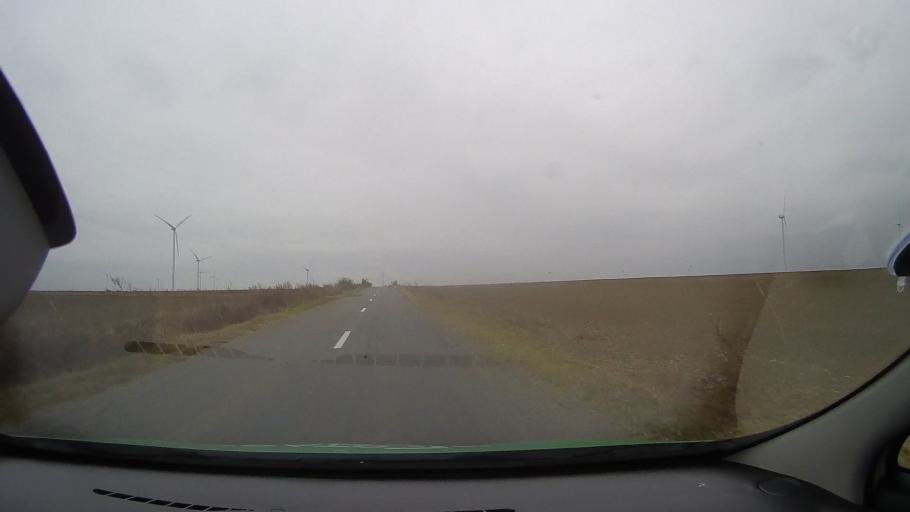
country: RO
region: Constanta
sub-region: Comuna Pantelimon
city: Pantelimon
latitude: 44.5077
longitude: 28.3435
